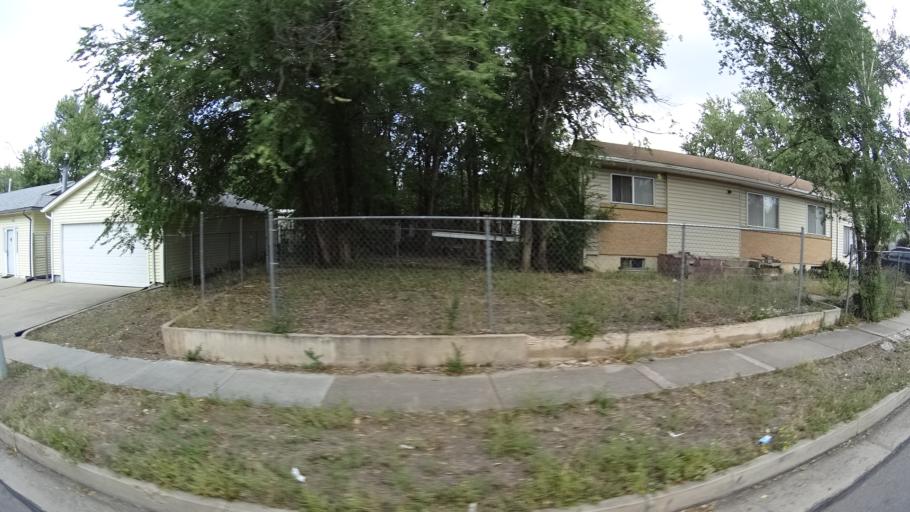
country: US
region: Colorado
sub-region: El Paso County
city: Cimarron Hills
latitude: 38.8512
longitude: -104.7608
